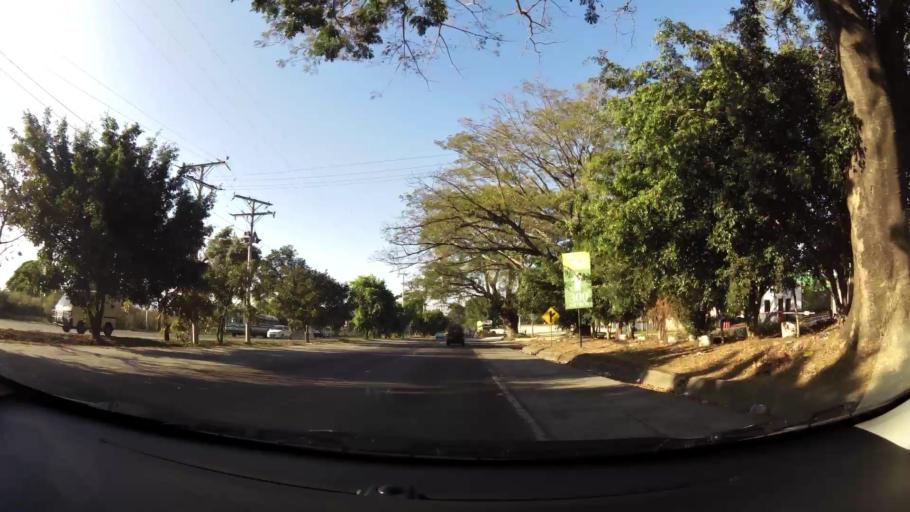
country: SV
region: La Libertad
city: Santa Tecla
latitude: 13.7405
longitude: -89.3622
